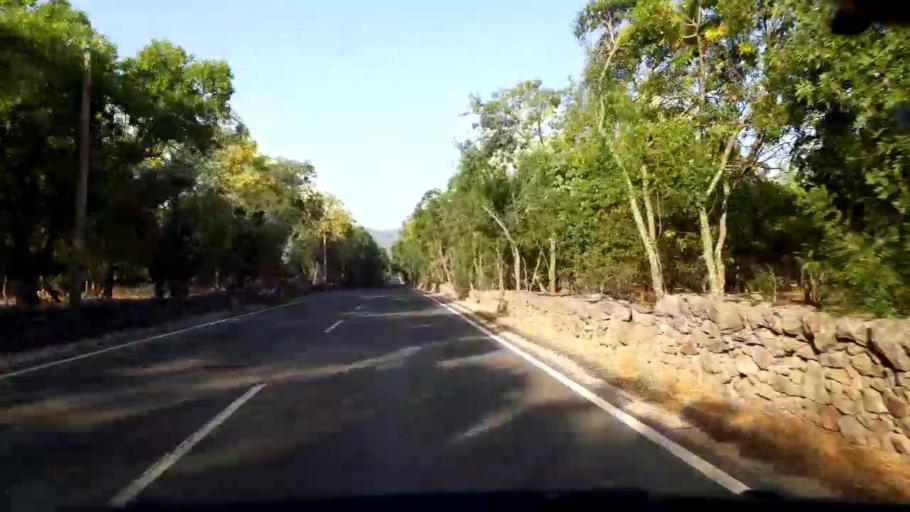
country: ES
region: Madrid
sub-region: Provincia de Madrid
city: Guadarrama
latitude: 40.6824
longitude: -4.0674
